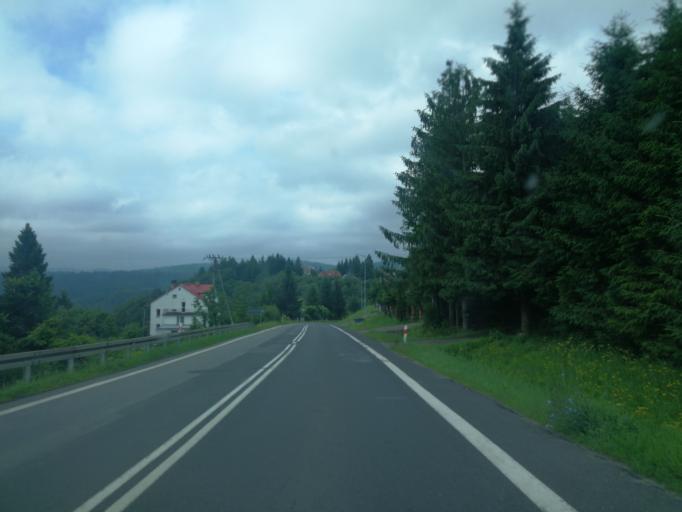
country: PL
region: Subcarpathian Voivodeship
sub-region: Powiat leski
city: Lesko
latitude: 49.4653
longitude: 22.3422
